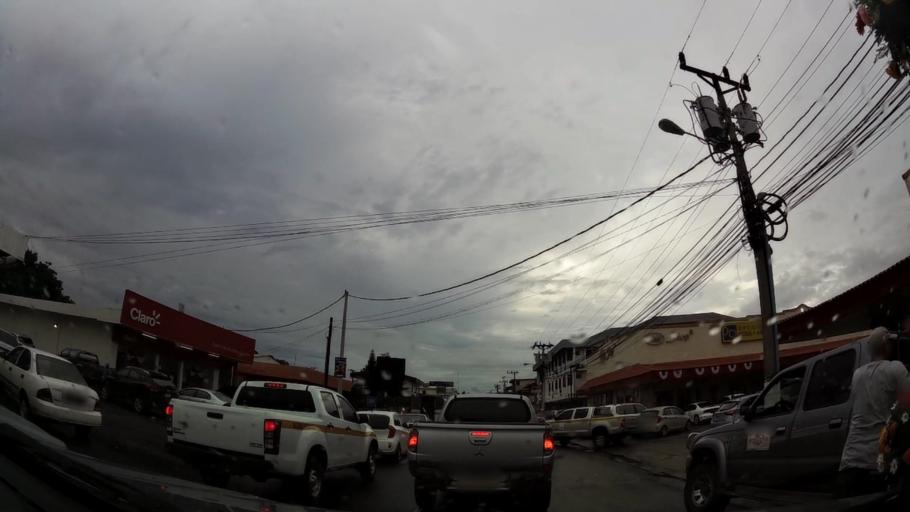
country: PA
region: Veraguas
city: Santiago de Veraguas
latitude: 8.0975
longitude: -80.9774
